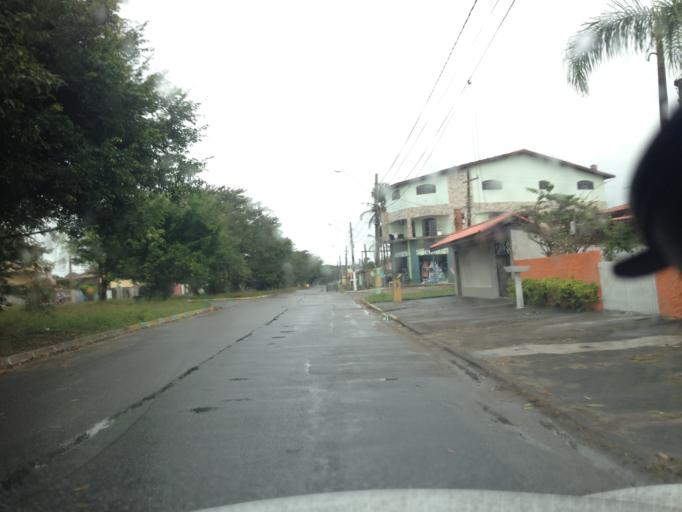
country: BR
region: Sao Paulo
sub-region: Itanhaem
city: Itanhaem
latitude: -24.2301
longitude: -46.8741
